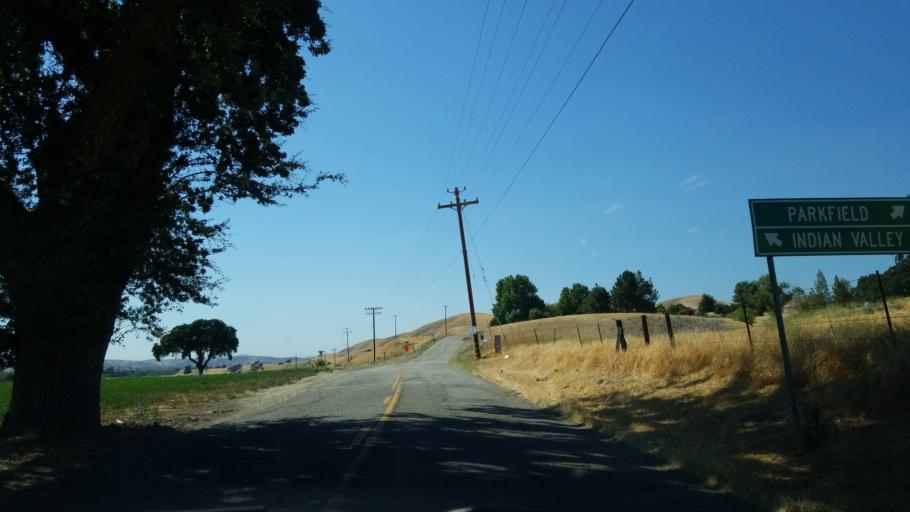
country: US
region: California
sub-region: San Luis Obispo County
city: San Miguel
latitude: 35.7724
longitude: -120.6922
